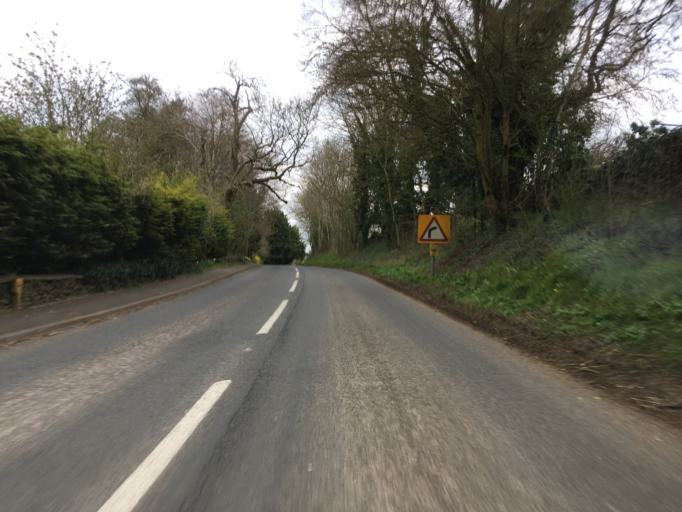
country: GB
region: England
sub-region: Gloucestershire
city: Northleach
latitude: 51.7867
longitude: -1.7758
